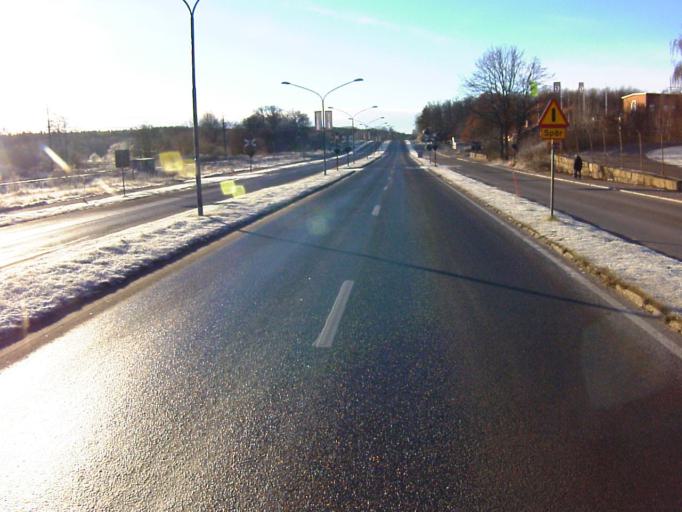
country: SE
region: Soedermanland
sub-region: Eskilstuna Kommun
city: Eskilstuna
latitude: 59.3505
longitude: 16.4966
